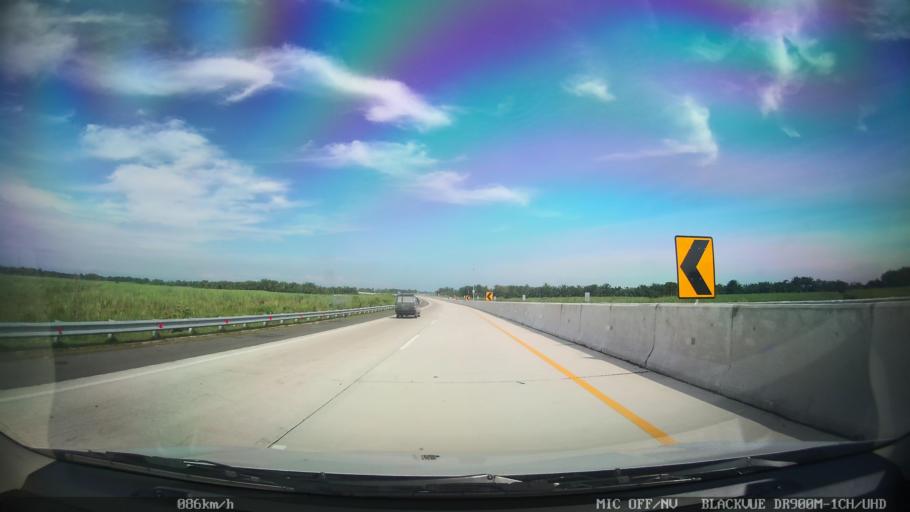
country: ID
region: North Sumatra
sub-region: Kabupaten Langkat
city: Stabat
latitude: 3.7089
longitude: 98.5345
